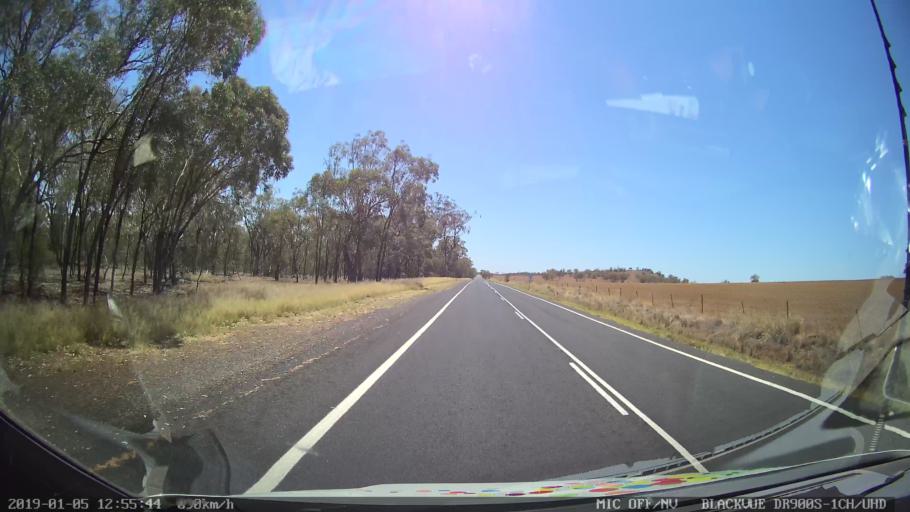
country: AU
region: New South Wales
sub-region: Warrumbungle Shire
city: Coonabarabran
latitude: -31.1196
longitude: 149.7104
